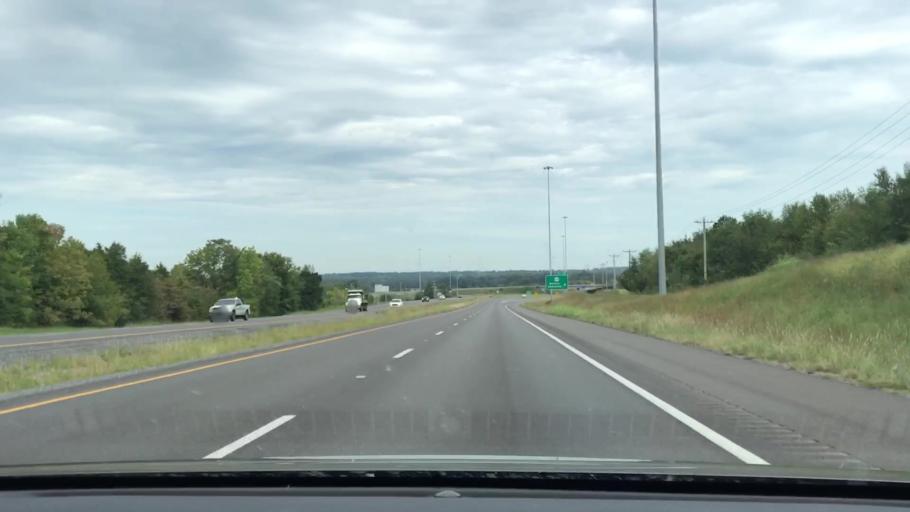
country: US
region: Kentucky
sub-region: Marshall County
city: Benton
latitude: 36.8621
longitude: -88.3669
